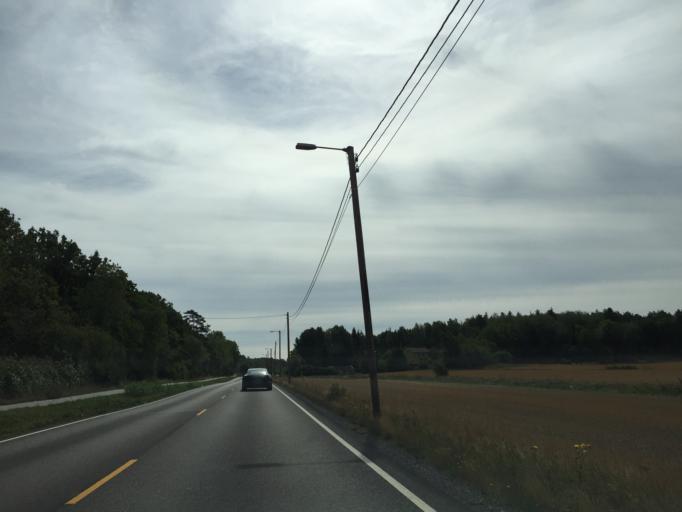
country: NO
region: Ostfold
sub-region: Fredrikstad
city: Fredrikstad
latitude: 59.1790
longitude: 10.9290
